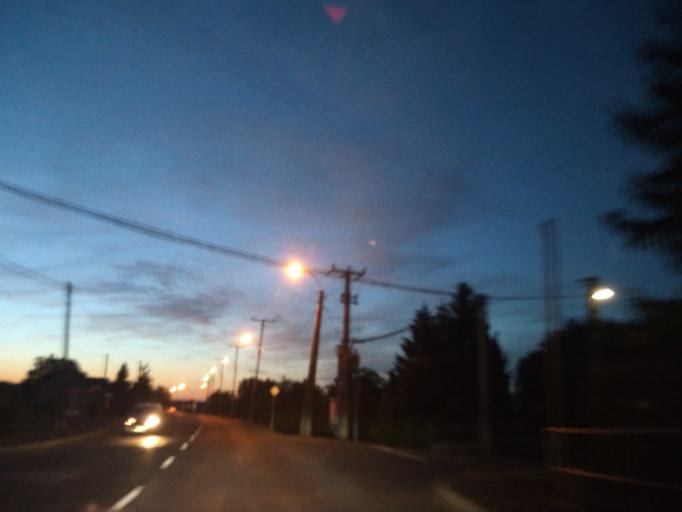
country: HU
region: Zala
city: Zalaegerszeg
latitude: 46.9432
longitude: 16.8497
